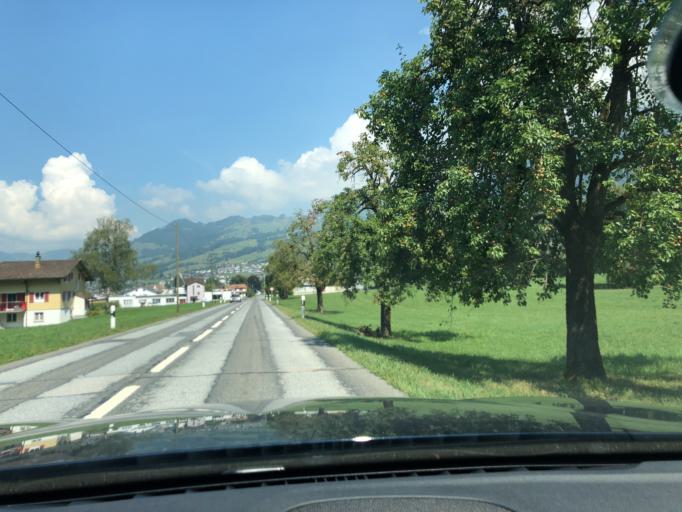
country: CH
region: Schwyz
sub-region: Bezirk Schwyz
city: Ibach
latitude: 47.0062
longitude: 8.6583
